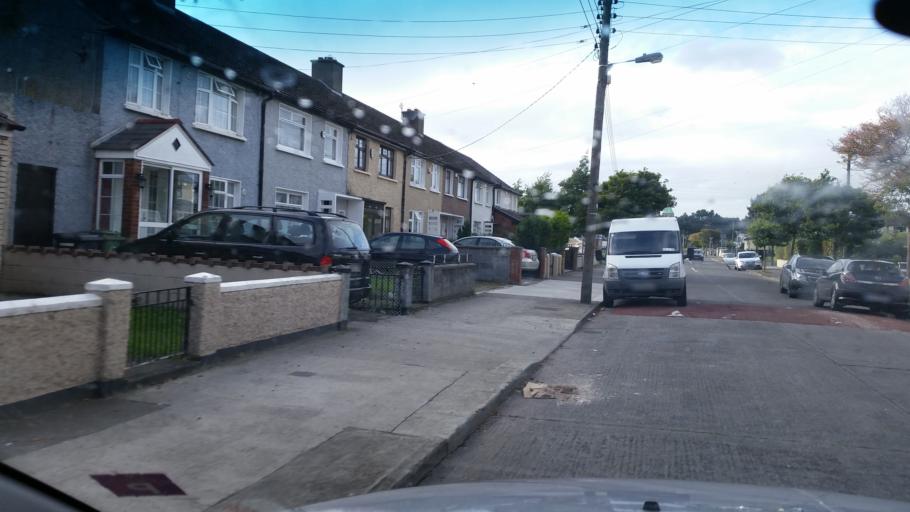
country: IE
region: Leinster
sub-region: Dublin City
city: Finglas
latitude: 53.3860
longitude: -6.2925
